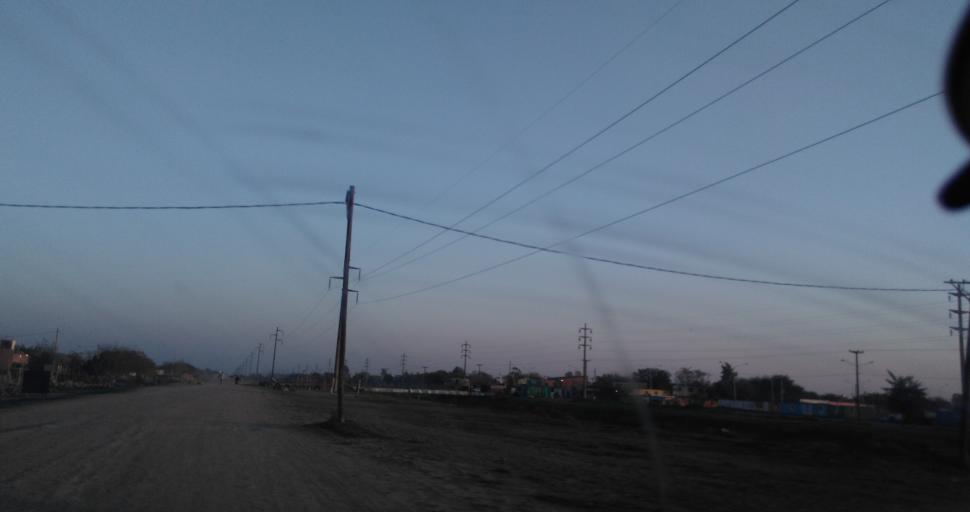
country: AR
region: Chaco
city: Resistencia
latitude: -27.4850
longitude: -58.9928
